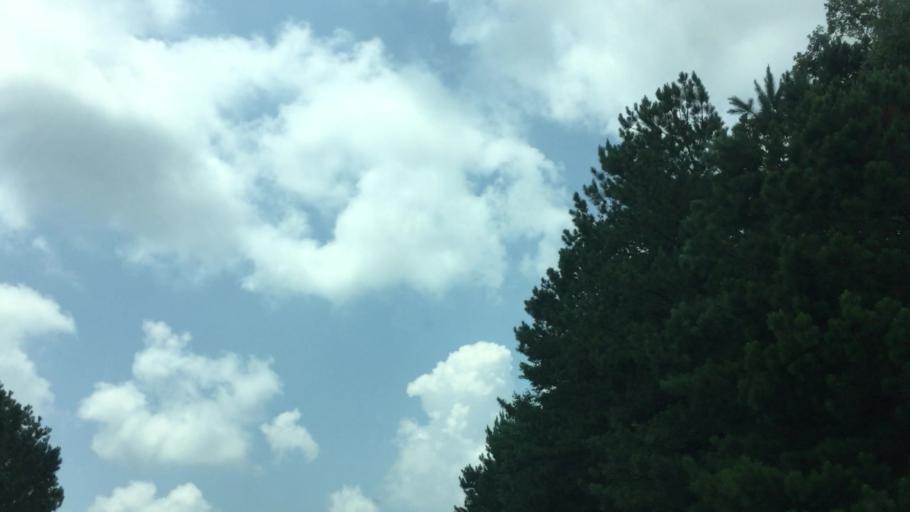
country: US
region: Georgia
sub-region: Fulton County
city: Chattahoochee Hills
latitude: 33.5636
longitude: -84.7498
